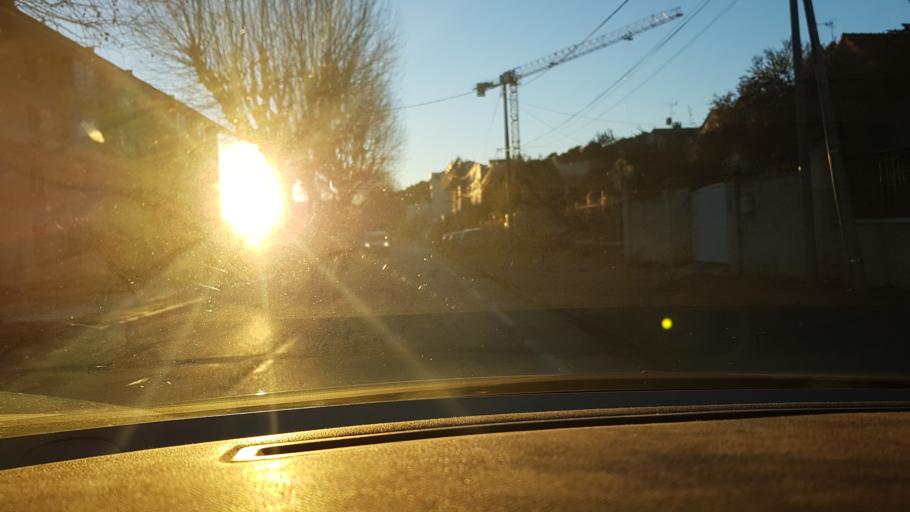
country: FR
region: Provence-Alpes-Cote d'Azur
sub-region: Departement des Bouches-du-Rhone
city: Gardanne
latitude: 43.4594
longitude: 5.4772
